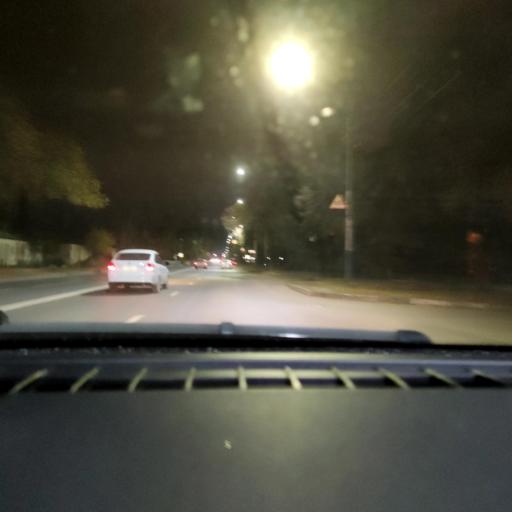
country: RU
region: Voronezj
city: Somovo
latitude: 51.7157
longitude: 39.2746
